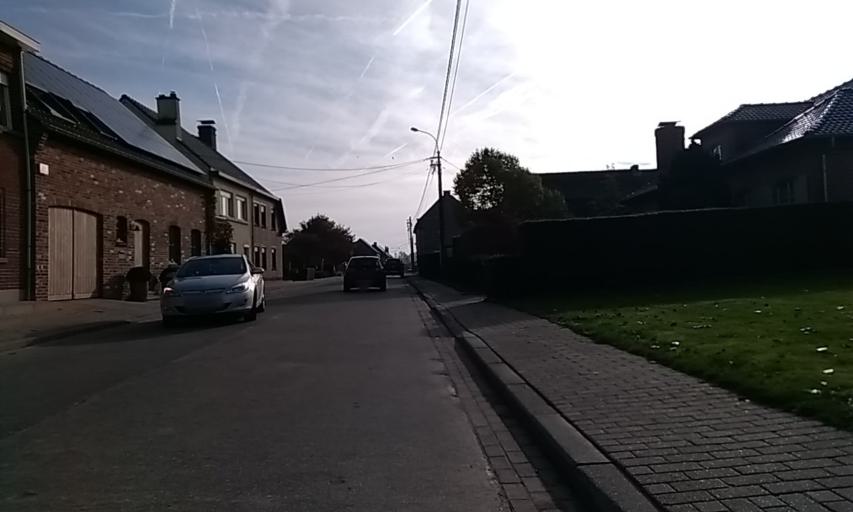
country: BE
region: Flanders
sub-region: Provincie Oost-Vlaanderen
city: Sint-Lievens-Houtem
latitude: 50.9233
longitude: 3.8407
